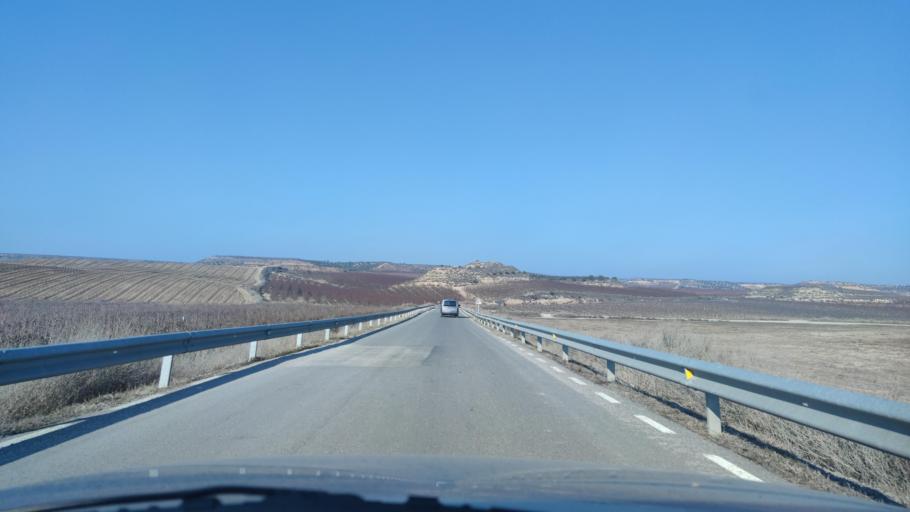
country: ES
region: Catalonia
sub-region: Provincia de Lleida
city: Sunyer
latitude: 41.5048
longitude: 0.5617
